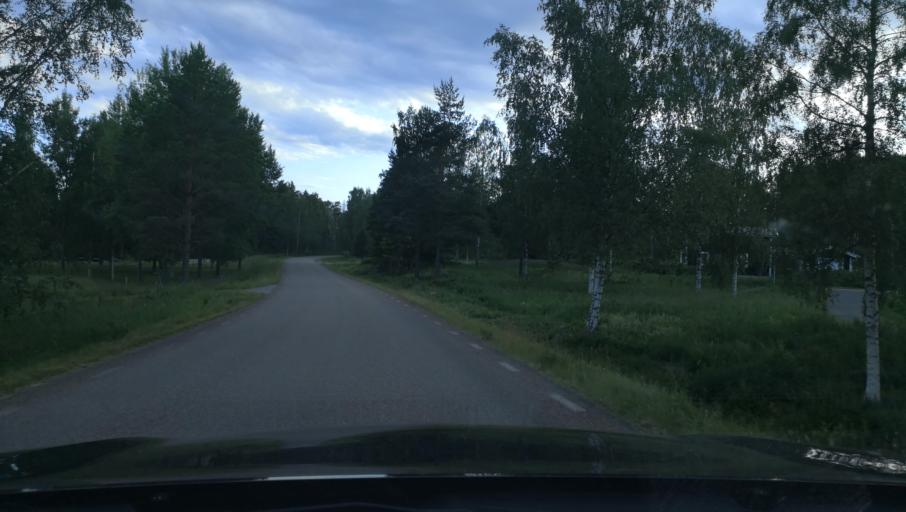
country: SE
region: Dalarna
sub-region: Ludvika Kommun
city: Ludvika
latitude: 60.1196
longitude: 15.2626
